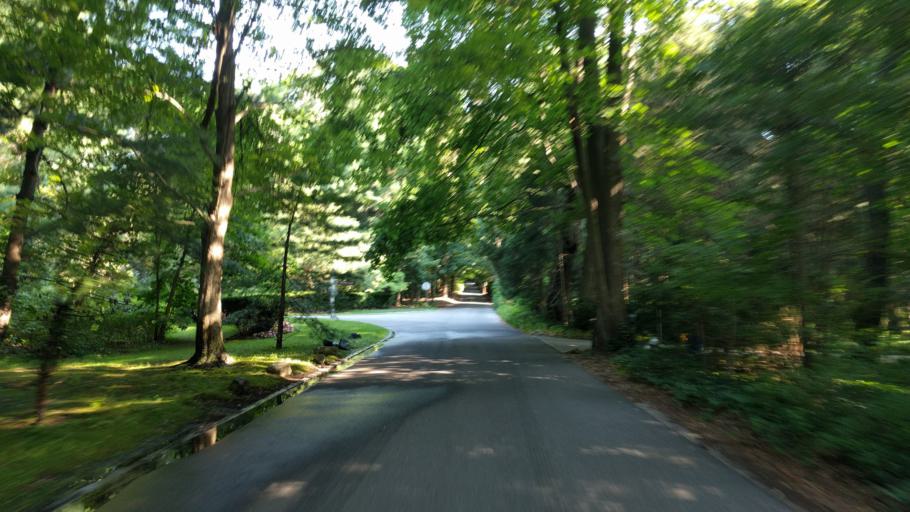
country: US
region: New York
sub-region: Nassau County
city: Lattingtown
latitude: 40.8933
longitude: -73.5879
